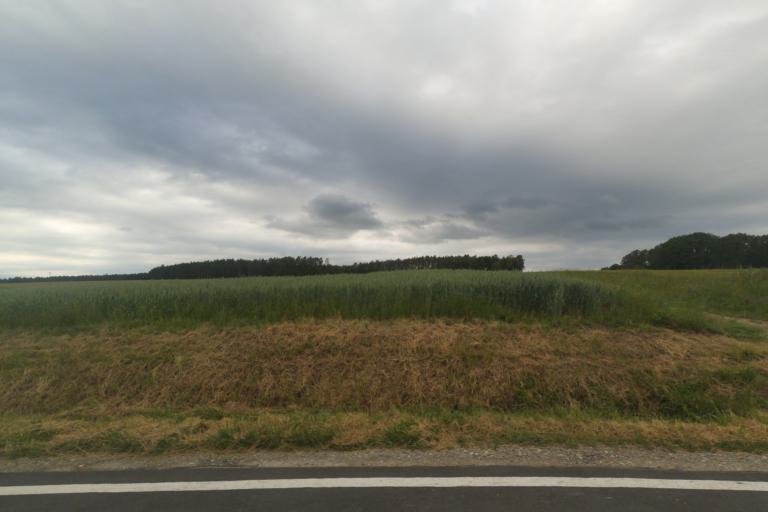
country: DE
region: Bavaria
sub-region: Regierungsbezirk Mittelfranken
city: Burghaslach
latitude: 49.7059
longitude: 10.5949
